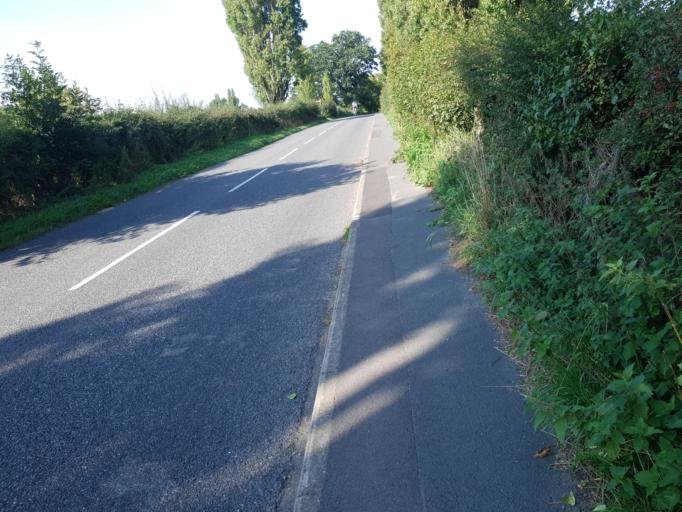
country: GB
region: England
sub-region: Suffolk
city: East Bergholt
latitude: 51.9471
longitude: 0.9956
